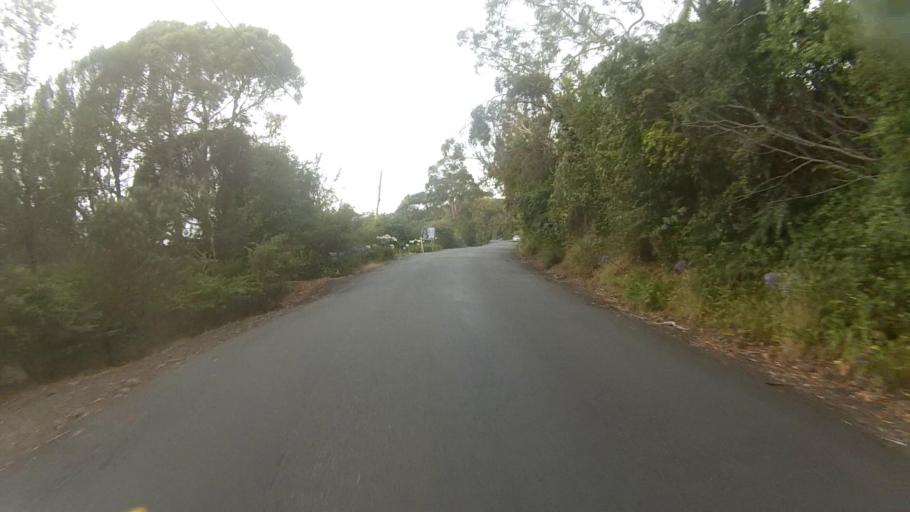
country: AU
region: Tasmania
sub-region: Hobart
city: Dynnyrne
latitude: -42.9084
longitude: 147.3257
